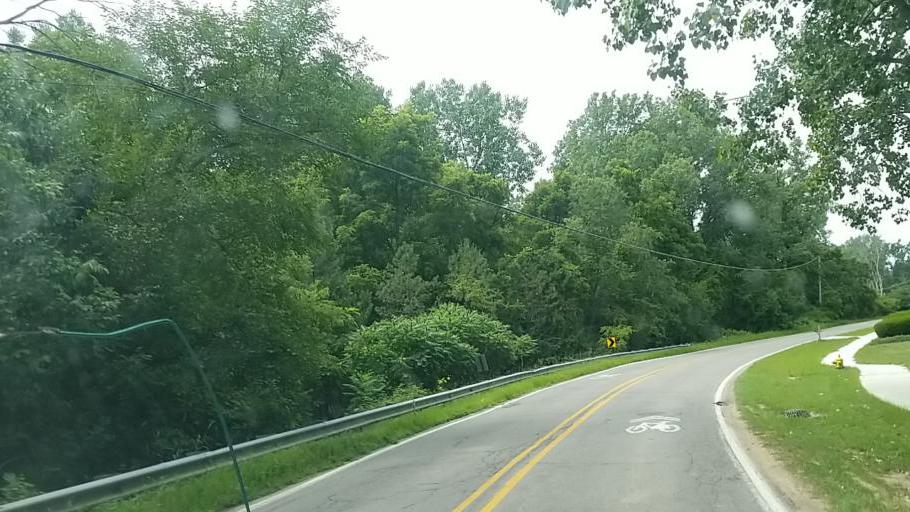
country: US
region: Michigan
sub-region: Kent County
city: Walker
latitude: 42.9992
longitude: -85.7360
